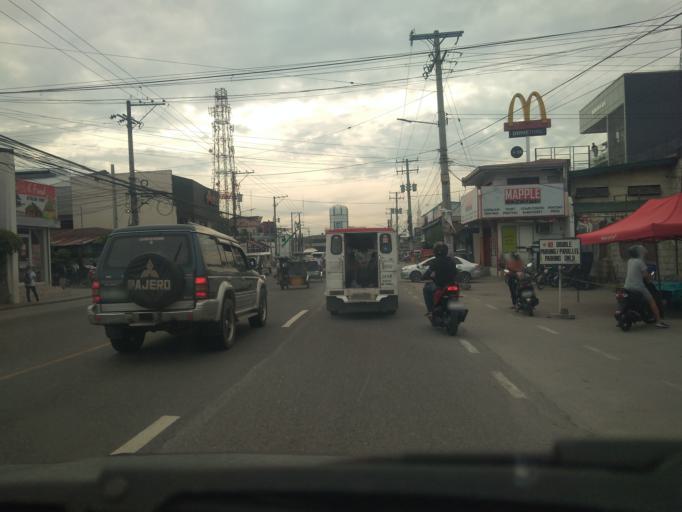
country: PH
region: Central Luzon
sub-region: Province of Pampanga
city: San Fernando
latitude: 15.0345
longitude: 120.6861
